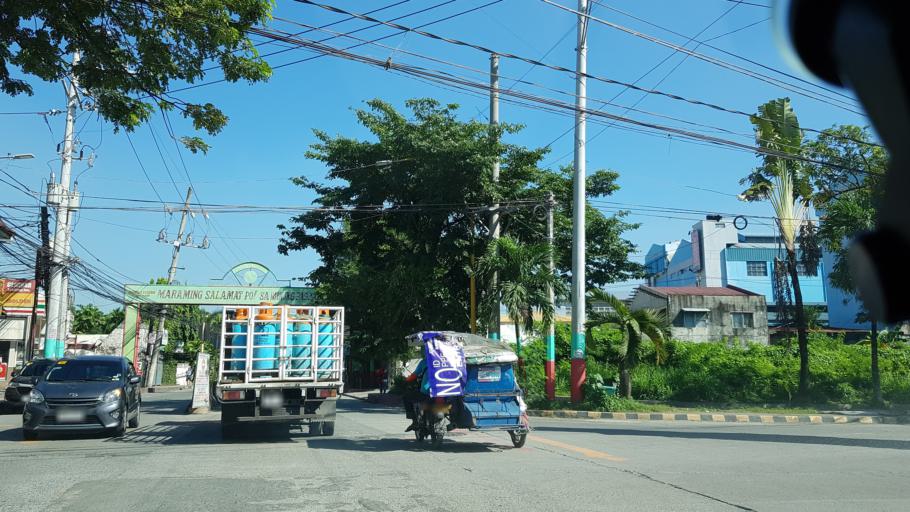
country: PH
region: Calabarzon
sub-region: Province of Rizal
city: Pateros
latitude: 14.5612
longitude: 121.0945
